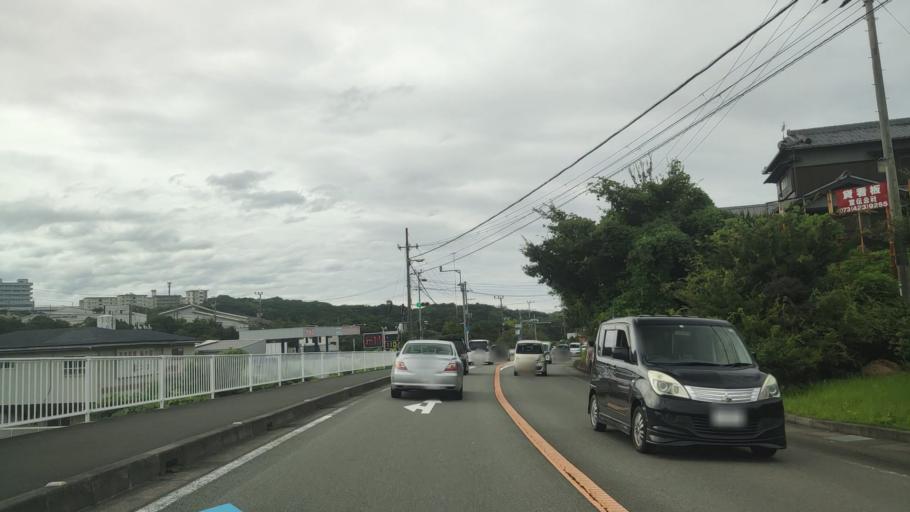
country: JP
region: Wakayama
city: Tanabe
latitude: 33.7065
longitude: 135.3996
